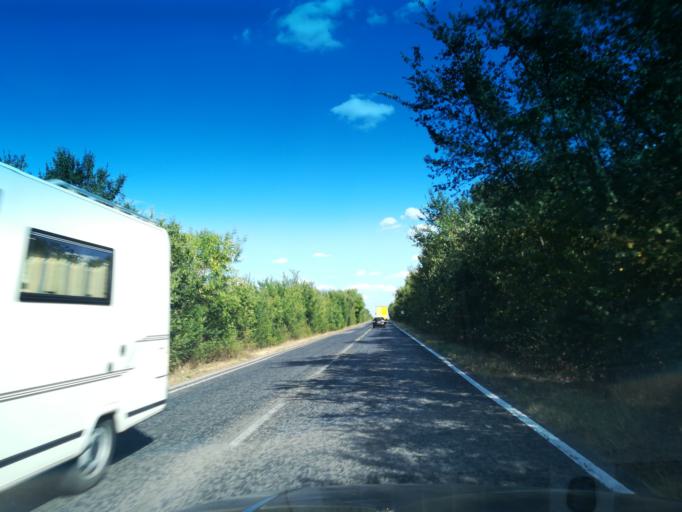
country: BG
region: Khaskovo
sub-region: Obshtina Mineralni Bani
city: Mineralni Bani
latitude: 42.0538
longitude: 25.3145
